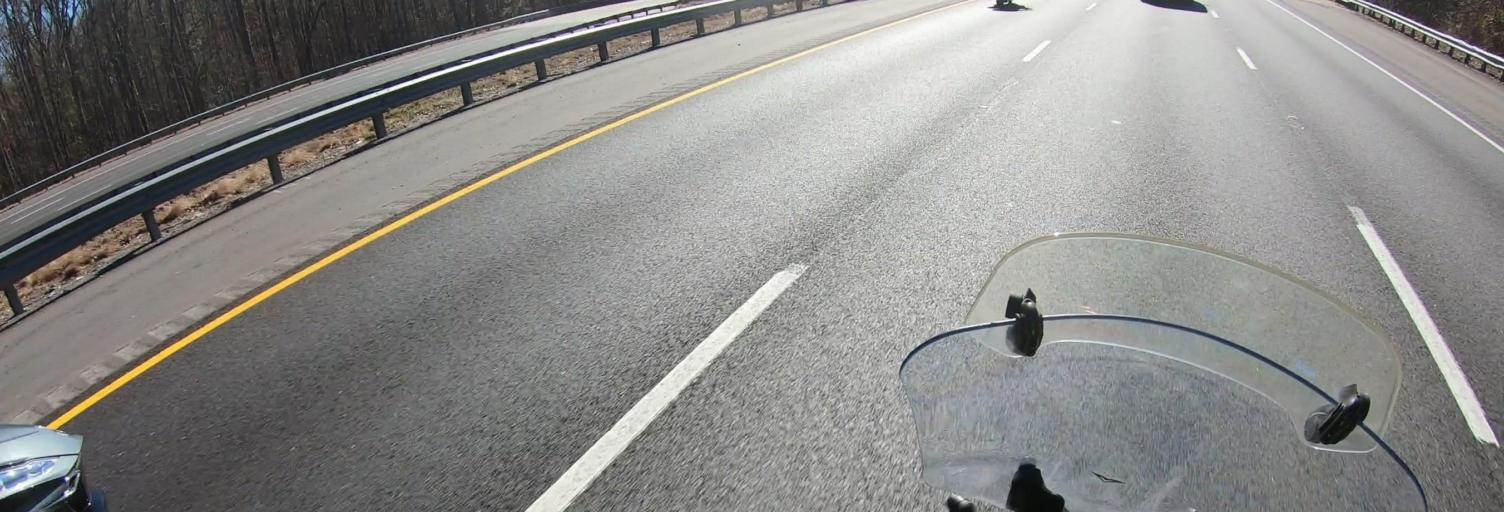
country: US
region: Georgia
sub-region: Bibb County
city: West Point
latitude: 32.7717
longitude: -83.7110
